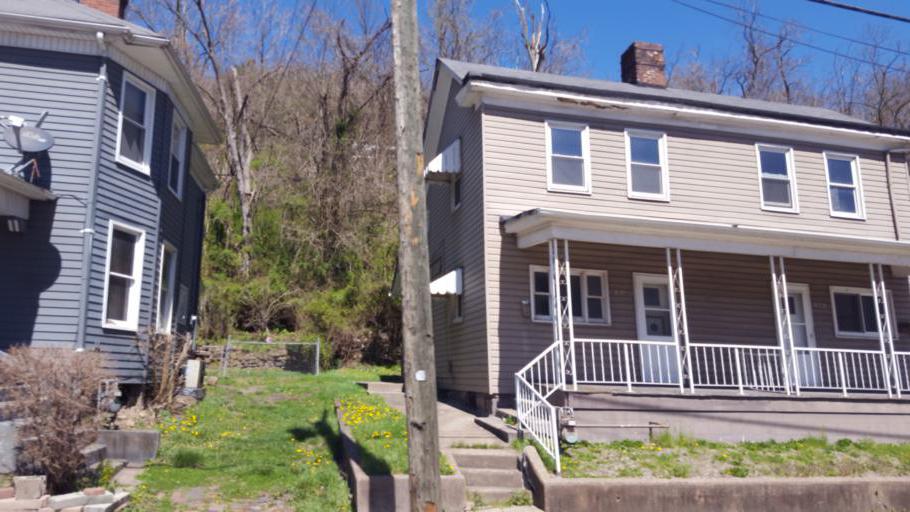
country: US
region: Ohio
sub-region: Belmont County
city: Bridgeport
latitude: 40.0707
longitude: -80.7559
